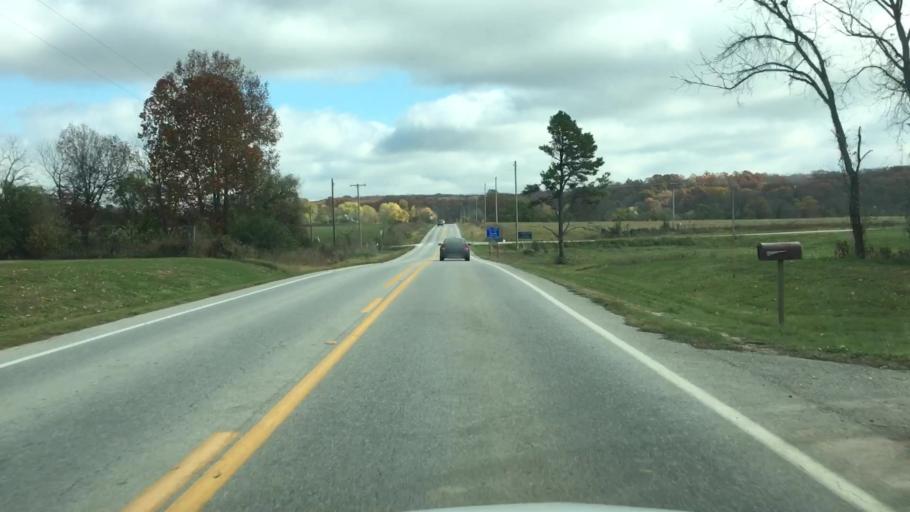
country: US
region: Arkansas
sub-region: Benton County
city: Gentry
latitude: 36.2558
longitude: -94.4422
